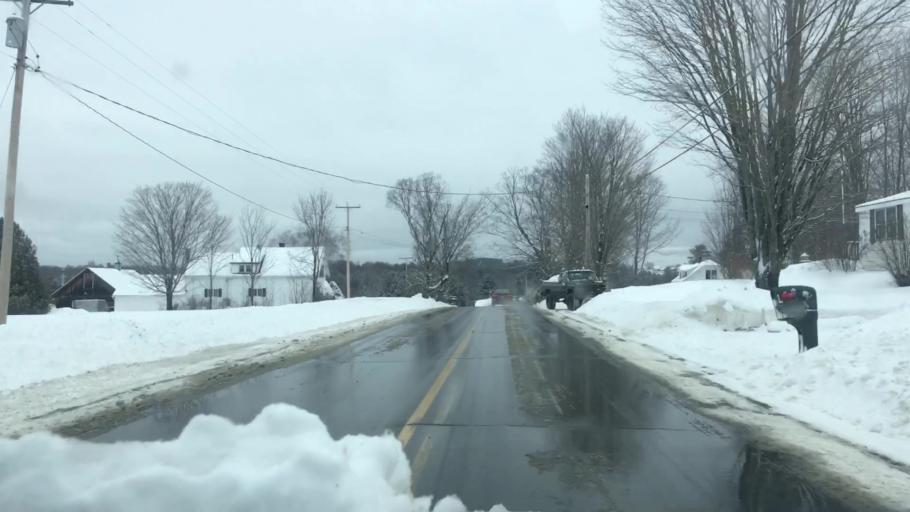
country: US
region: Maine
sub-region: Penobscot County
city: Charleston
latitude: 44.9959
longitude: -69.0444
